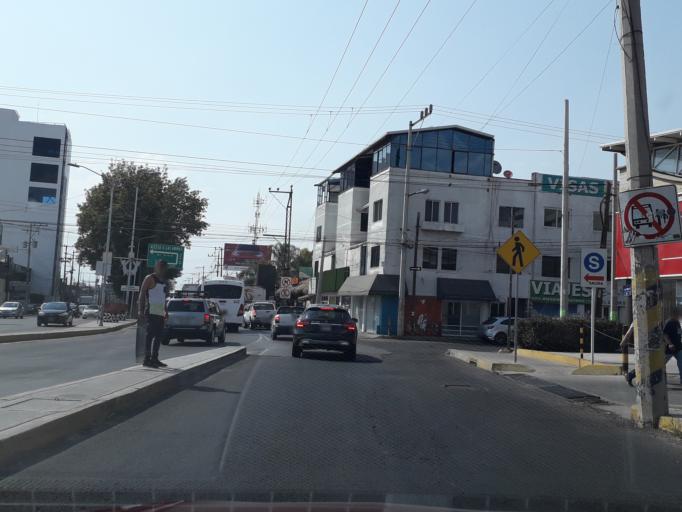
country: MX
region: Puebla
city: Puebla
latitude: 19.0395
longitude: -98.2263
